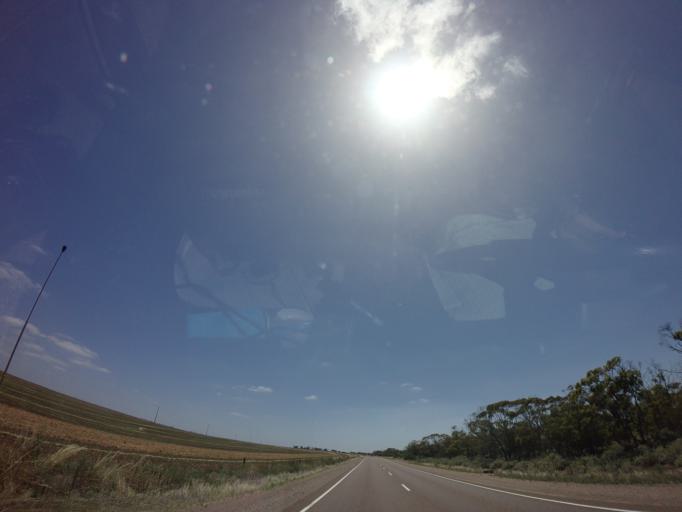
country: AU
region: South Australia
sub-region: Kimba
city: Caralue
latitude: -33.1988
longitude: 136.3679
